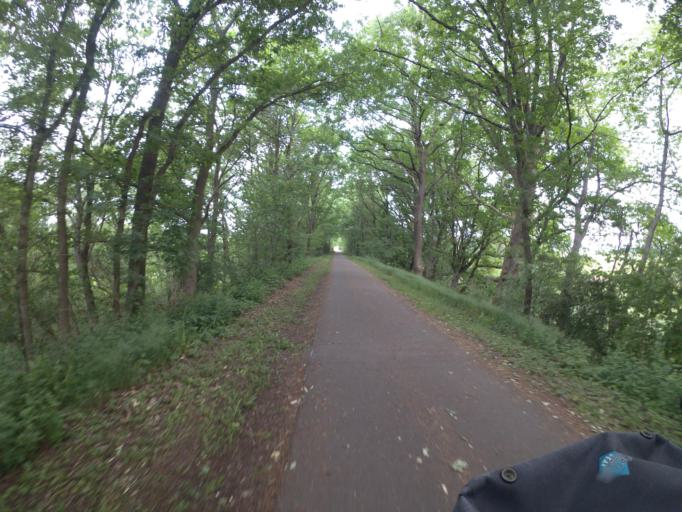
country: DE
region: Rheinland-Pfalz
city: Weilerbach
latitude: 49.4816
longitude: 7.6179
